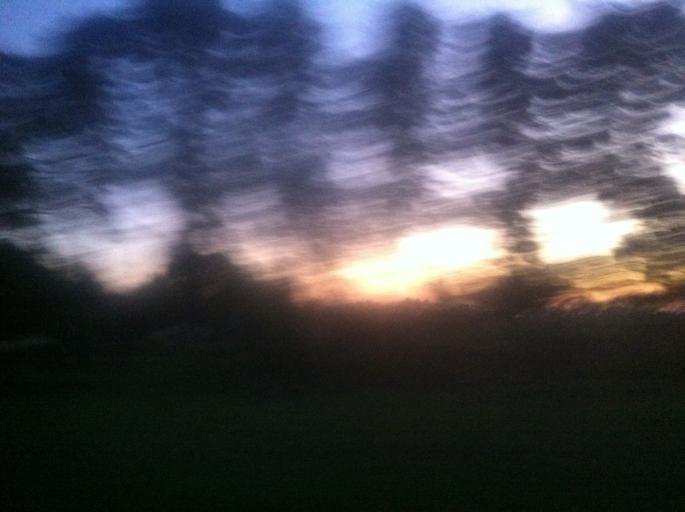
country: PY
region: Misiones
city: San Patricio
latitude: -26.9604
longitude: -56.8377
